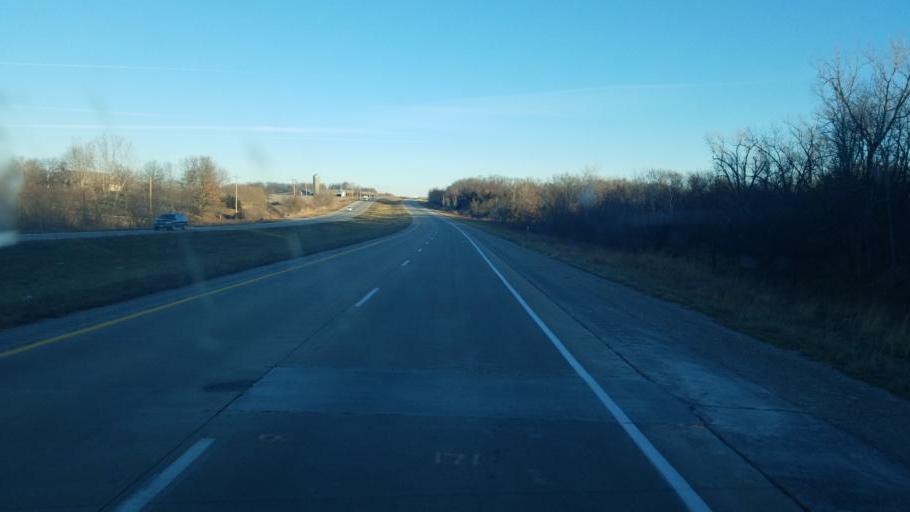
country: US
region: Iowa
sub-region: Wapello County
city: Eddyville
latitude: 41.2069
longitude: -92.6399
